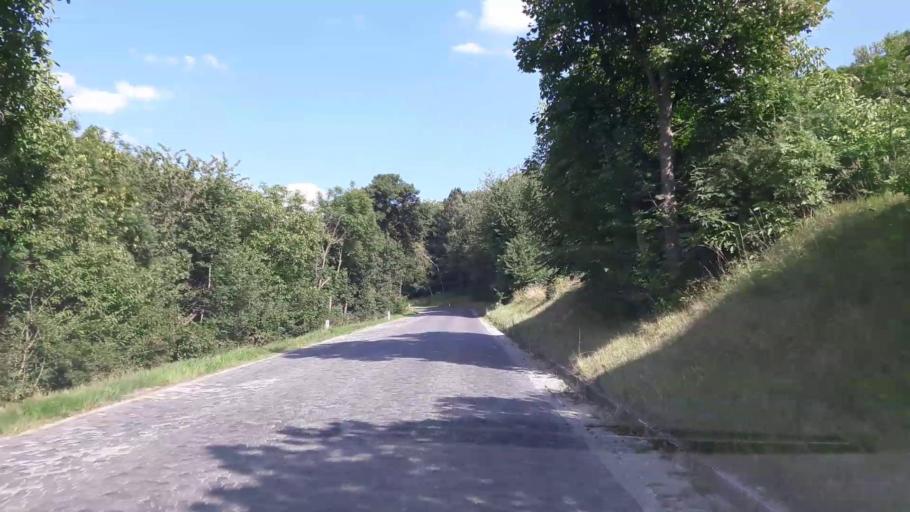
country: AT
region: Lower Austria
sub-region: Politischer Bezirk Wien-Umgebung
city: Klosterneuburg
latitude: 48.2864
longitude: 16.3238
